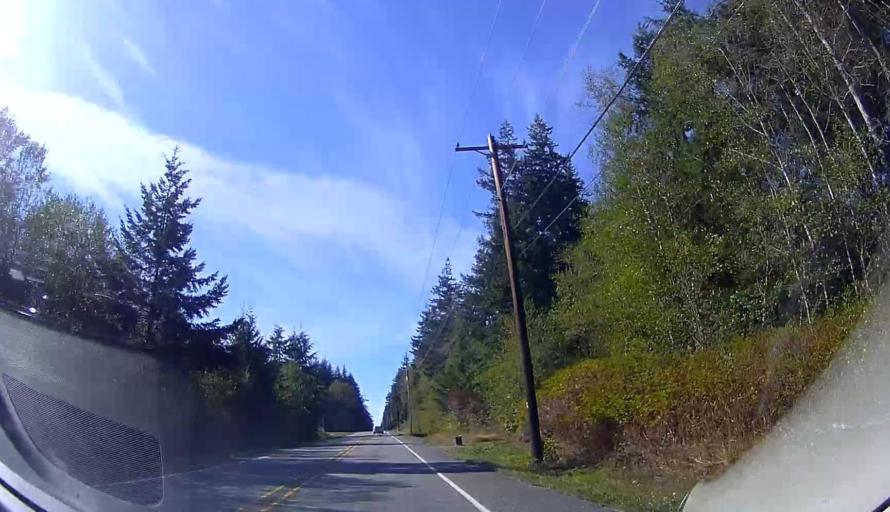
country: US
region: Washington
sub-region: Island County
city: Camano
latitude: 48.2254
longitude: -122.4932
